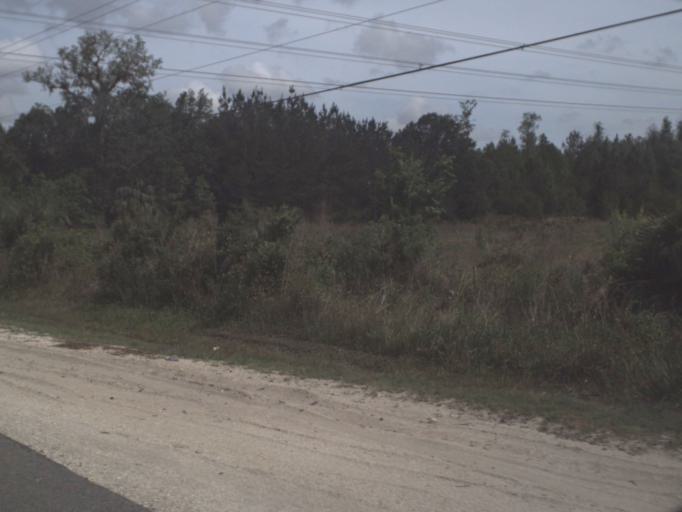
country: US
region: Florida
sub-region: Flagler County
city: Bunnell
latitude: 29.4669
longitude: -81.2873
